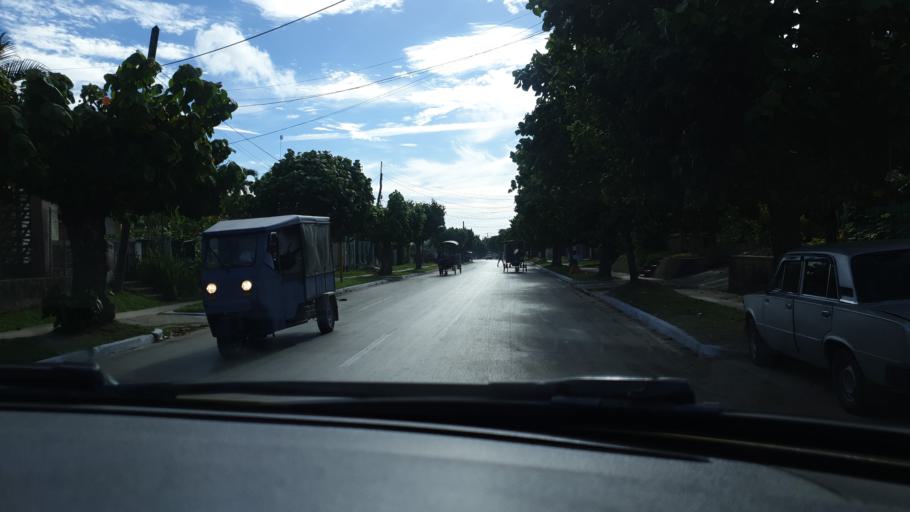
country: CU
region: Villa Clara
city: Santa Clara
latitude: 22.4132
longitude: -79.9525
